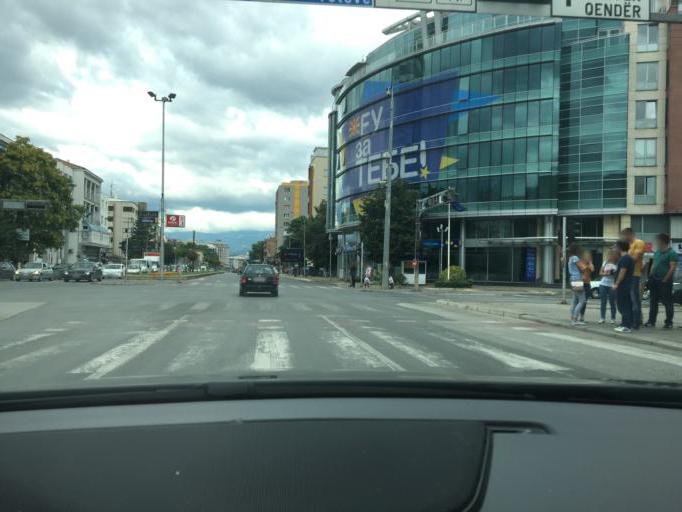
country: MK
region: Karpos
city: Skopje
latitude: 41.9930
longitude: 21.4244
